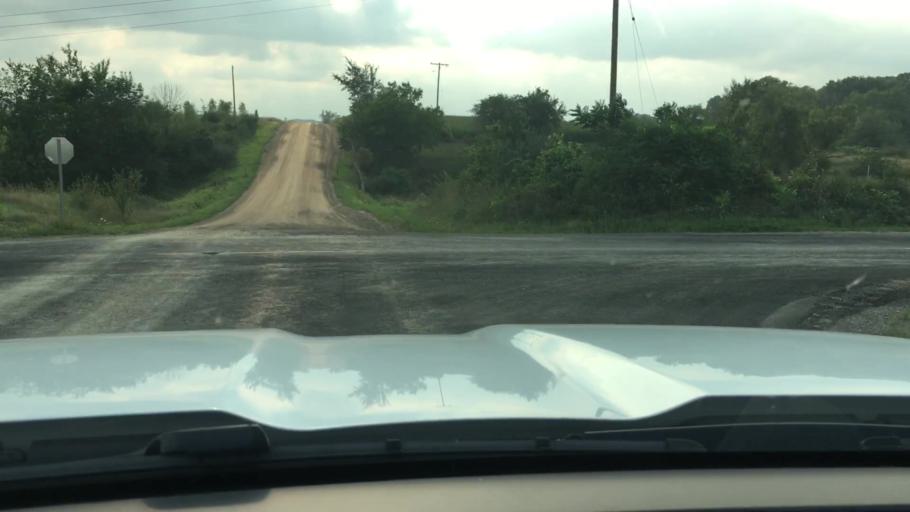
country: US
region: Michigan
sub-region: Ottawa County
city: Hudsonville
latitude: 42.8329
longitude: -85.8814
